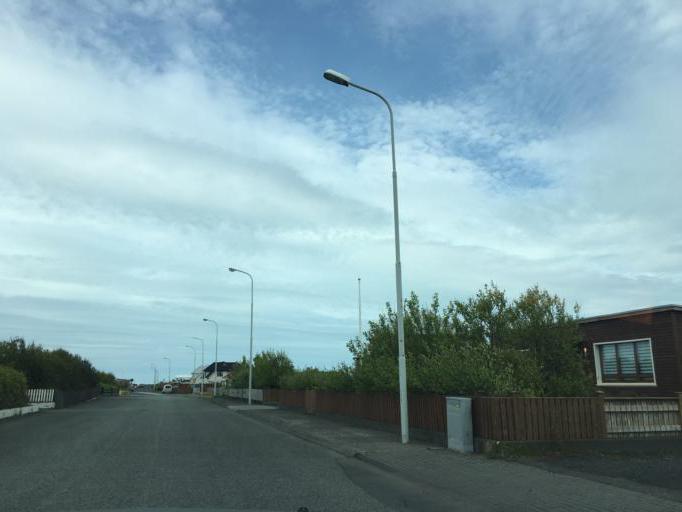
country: IS
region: Southern Peninsula
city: Reykjanesbaer
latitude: 63.9762
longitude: -22.5078
